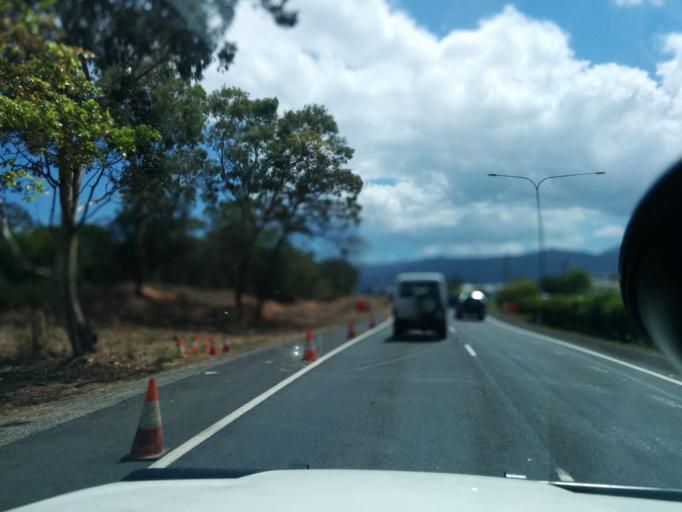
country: AU
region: Queensland
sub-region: Cairns
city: Woree
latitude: -16.9443
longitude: 145.7632
